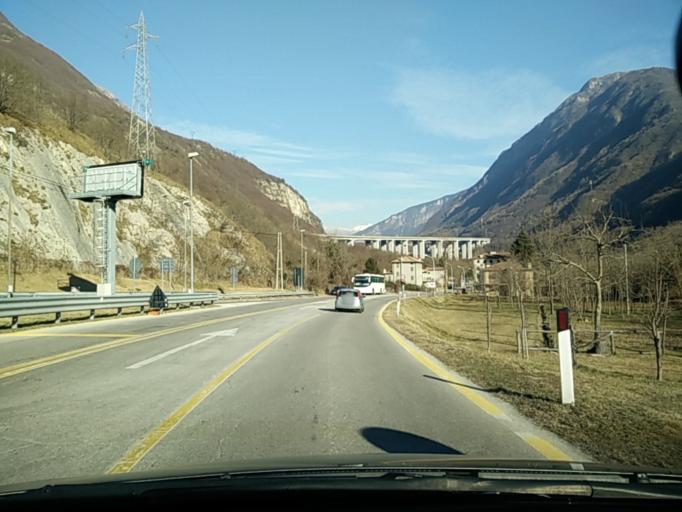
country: IT
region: Veneto
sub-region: Provincia di Treviso
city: Revine
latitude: 46.0206
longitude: 12.2915
